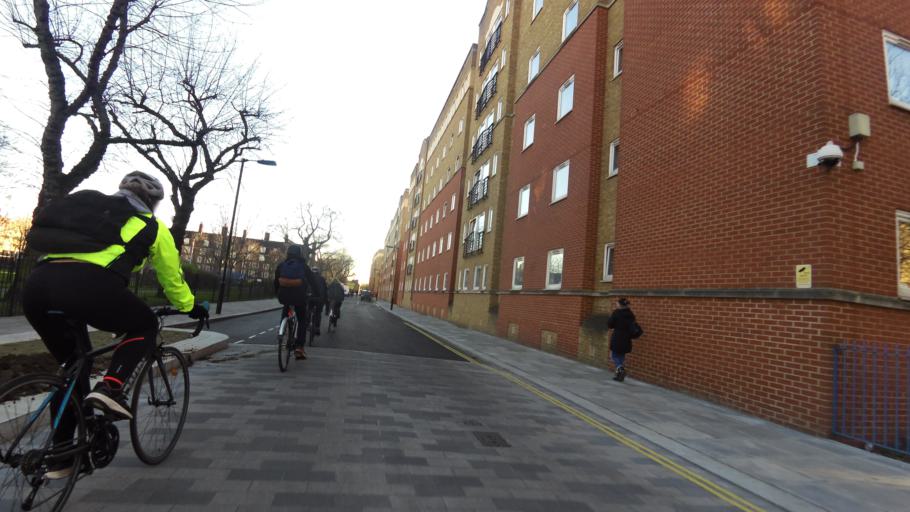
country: GB
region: England
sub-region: Greater London
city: City of London
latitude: 51.4986
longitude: -0.0898
